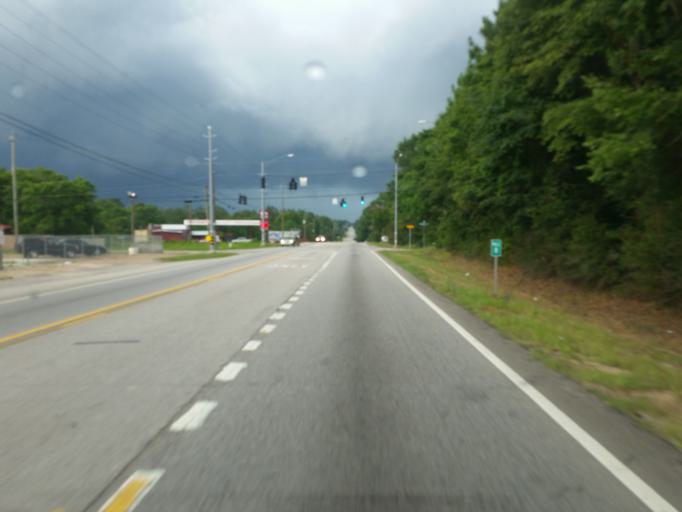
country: US
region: Mississippi
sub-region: Jackson County
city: Hurley
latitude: 30.7962
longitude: -88.3197
